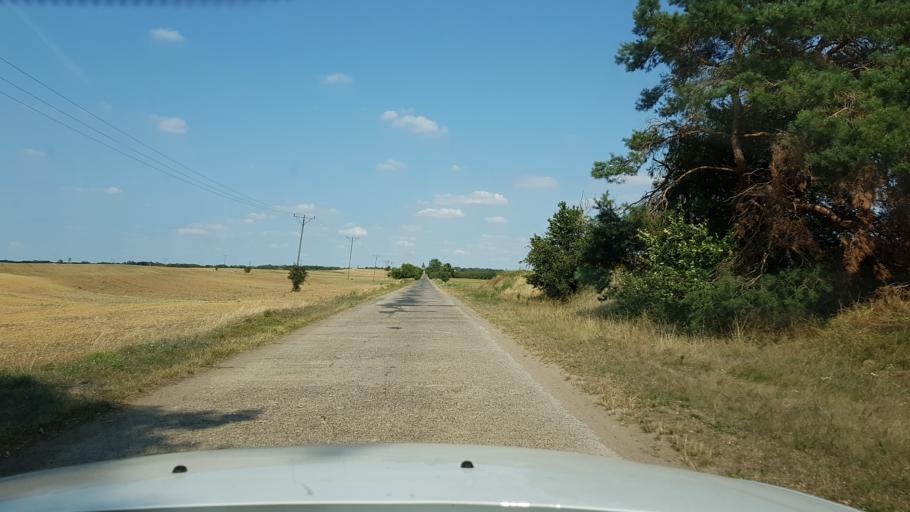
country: PL
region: West Pomeranian Voivodeship
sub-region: Powiat gryfinski
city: Moryn
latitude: 52.8397
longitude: 14.3831
